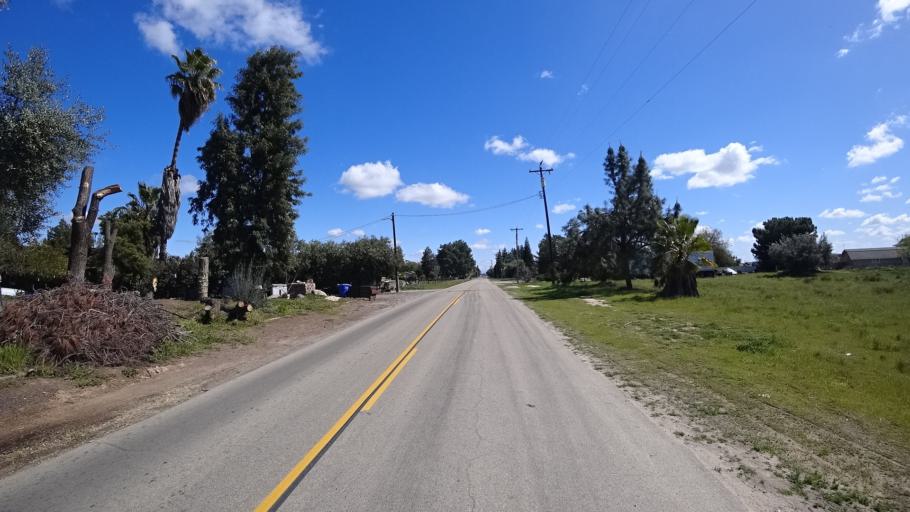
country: US
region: California
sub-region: Fresno County
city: Biola
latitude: 36.8223
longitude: -119.9255
